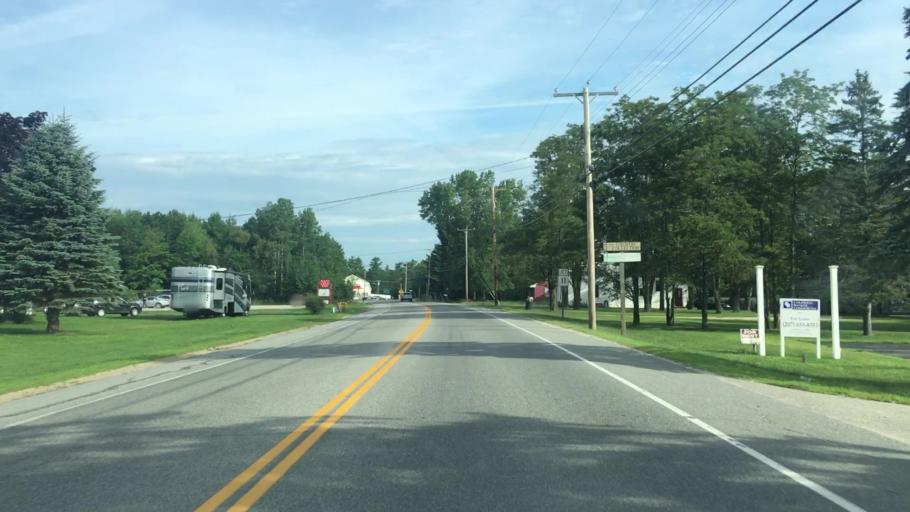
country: US
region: Maine
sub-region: York County
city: Limington
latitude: 43.7440
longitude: -70.6760
